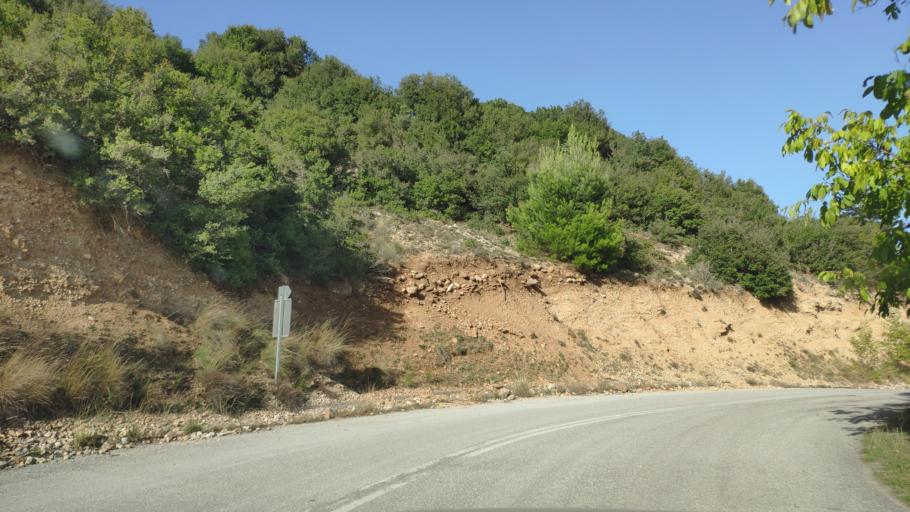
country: GR
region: West Greece
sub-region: Nomos Achaias
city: Aiyira
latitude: 37.9903
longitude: 22.3631
